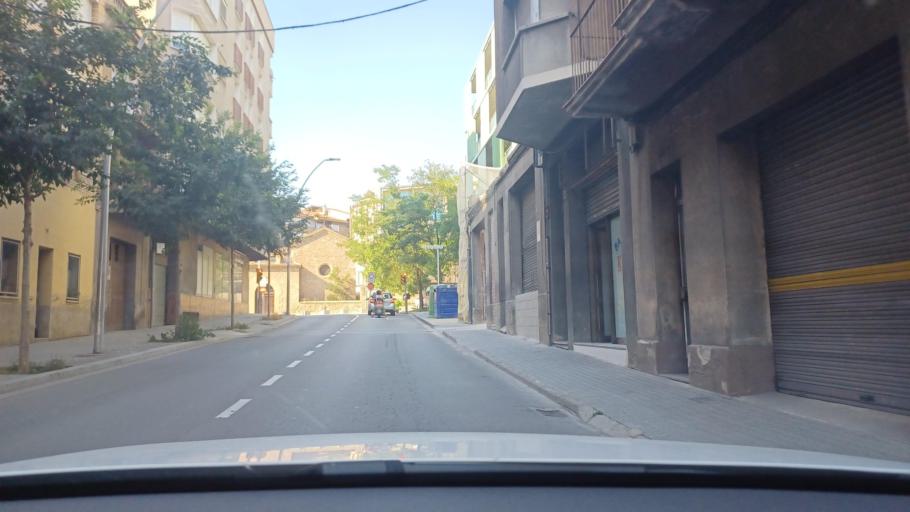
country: ES
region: Catalonia
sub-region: Provincia de Barcelona
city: Manresa
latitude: 41.7238
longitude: 1.8287
